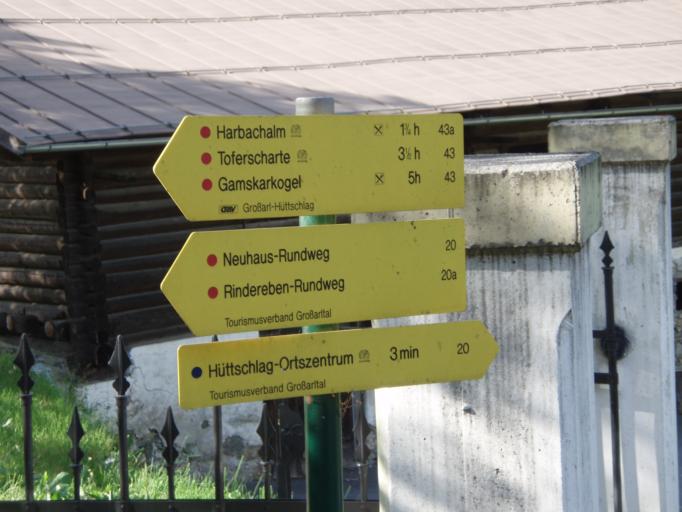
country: AT
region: Salzburg
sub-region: Politischer Bezirk Sankt Johann im Pongau
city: Huttschlag
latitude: 47.1785
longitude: 13.2276
